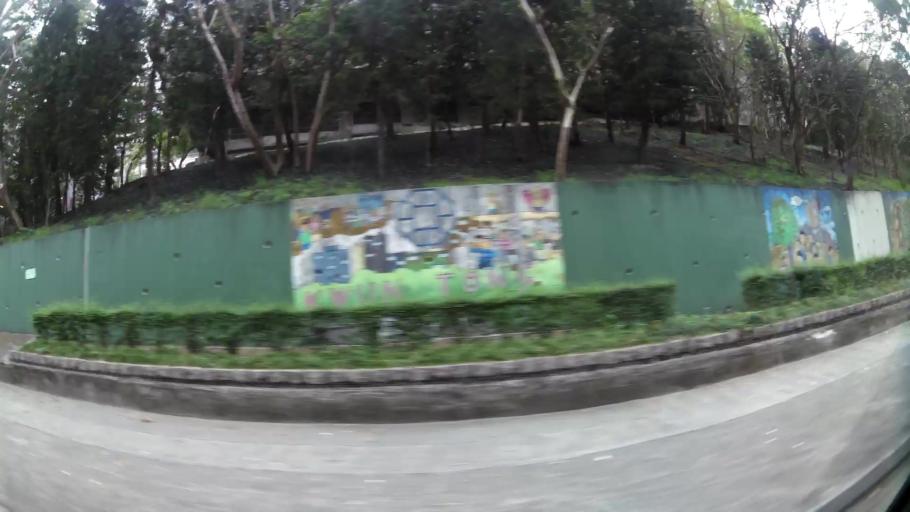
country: HK
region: Kowloon City
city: Kowloon
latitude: 22.3257
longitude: 114.2246
